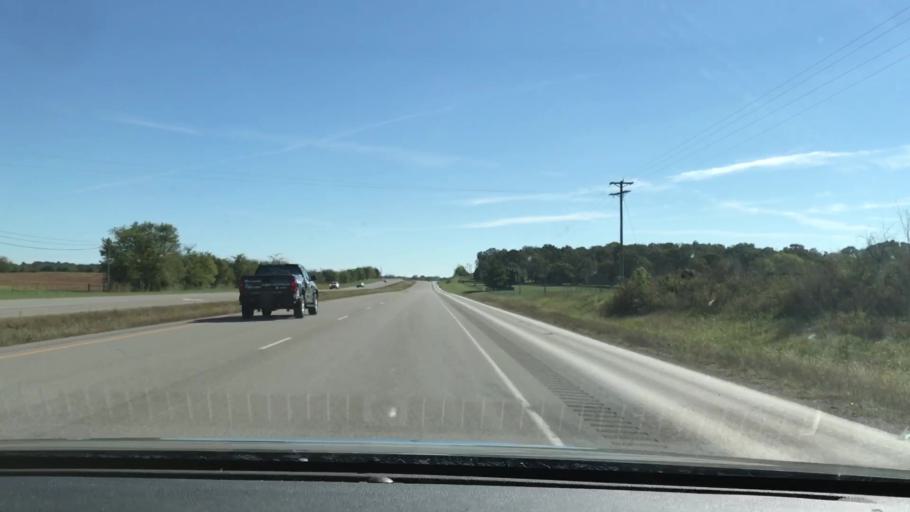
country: US
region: Kentucky
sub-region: Christian County
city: Hopkinsville
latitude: 36.8496
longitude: -87.3490
